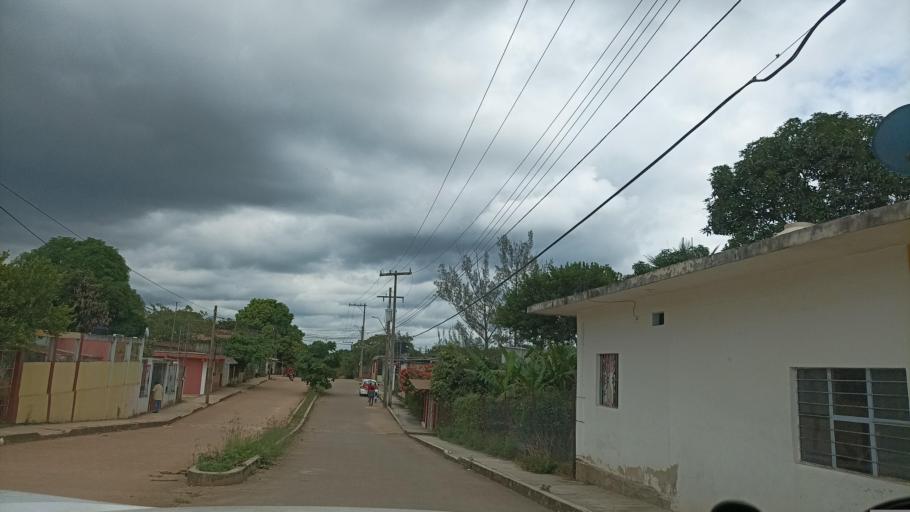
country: MX
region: Veracruz
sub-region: Soconusco
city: Colonia Lealtad
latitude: 17.9614
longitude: -94.8986
